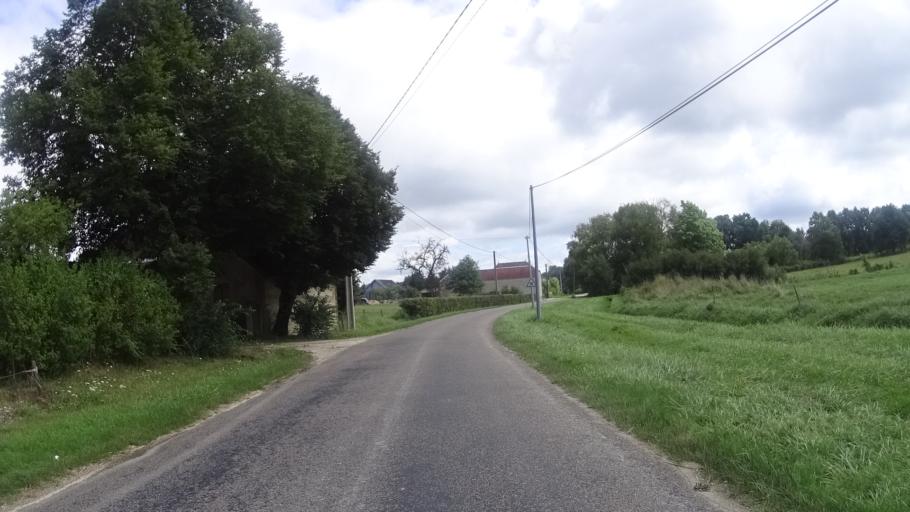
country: FR
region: Champagne-Ardenne
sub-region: Departement de l'Aube
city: Ervy-le-Chatel
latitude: 48.0740
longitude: 3.9624
